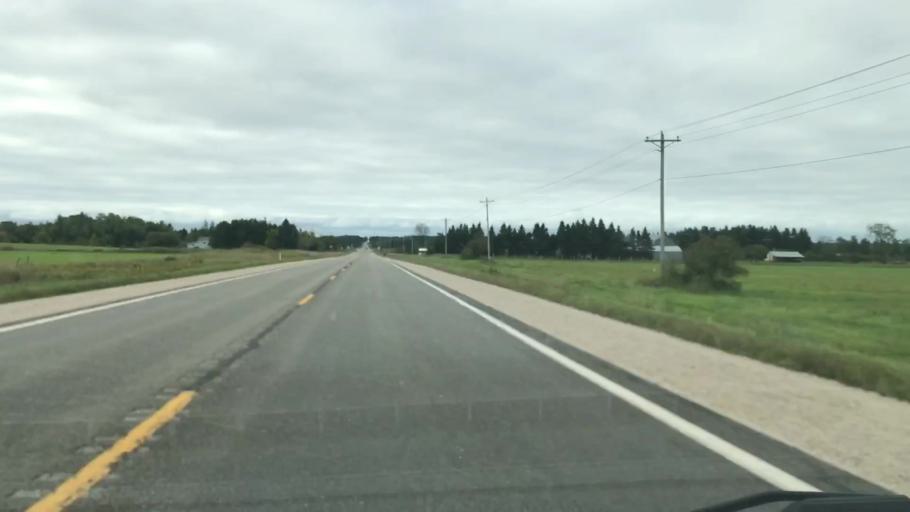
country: US
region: Michigan
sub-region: Luce County
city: Newberry
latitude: 46.1531
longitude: -85.5715
